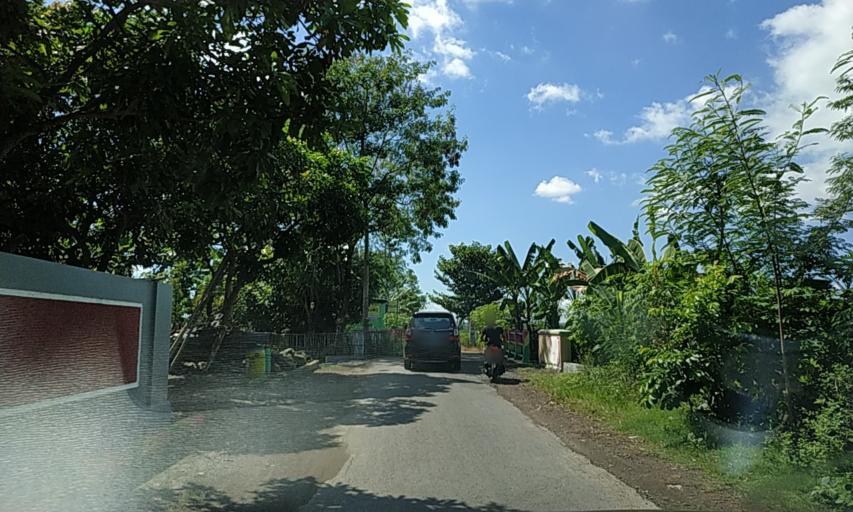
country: ID
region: Central Java
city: Trucuk
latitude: -7.7353
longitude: 110.7227
